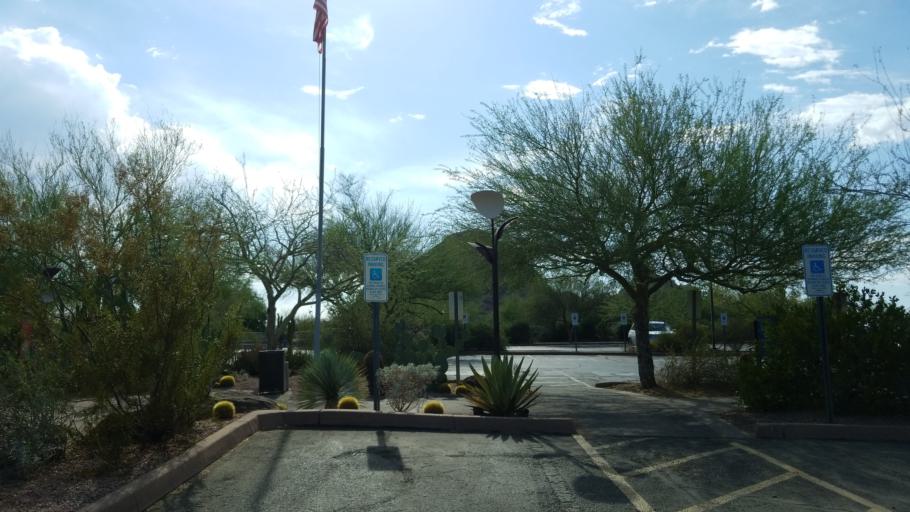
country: US
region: Arizona
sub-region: Maricopa County
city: Tempe Junction
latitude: 33.4626
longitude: -111.9444
